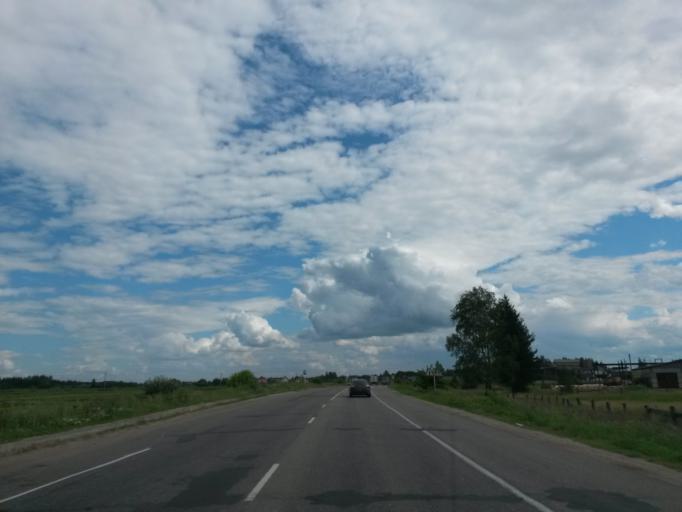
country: RU
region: Ivanovo
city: Novo-Talitsy
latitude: 57.0125
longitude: 40.8268
